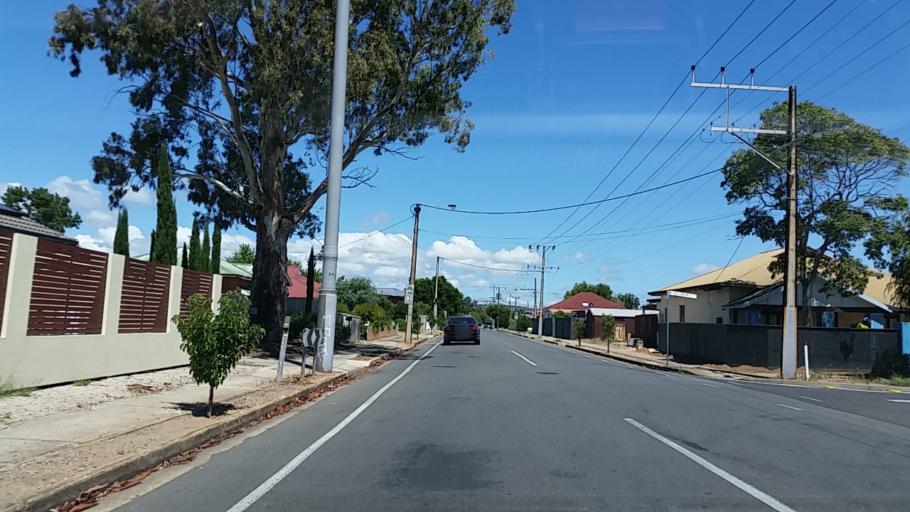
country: AU
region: South Australia
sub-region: Marion
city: South Plympton
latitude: -34.9839
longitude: 138.5652
